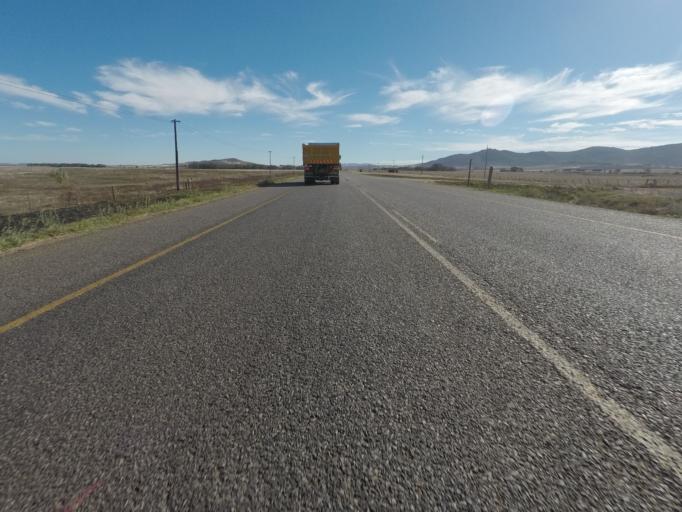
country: ZA
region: Western Cape
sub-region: West Coast District Municipality
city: Malmesbury
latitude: -33.6295
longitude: 18.7228
